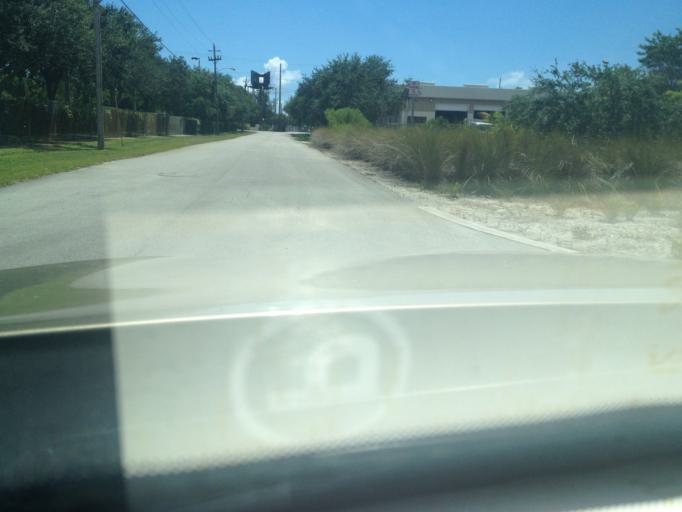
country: US
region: Florida
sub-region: Palm Beach County
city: Hypoluxo
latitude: 26.5560
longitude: -80.0732
